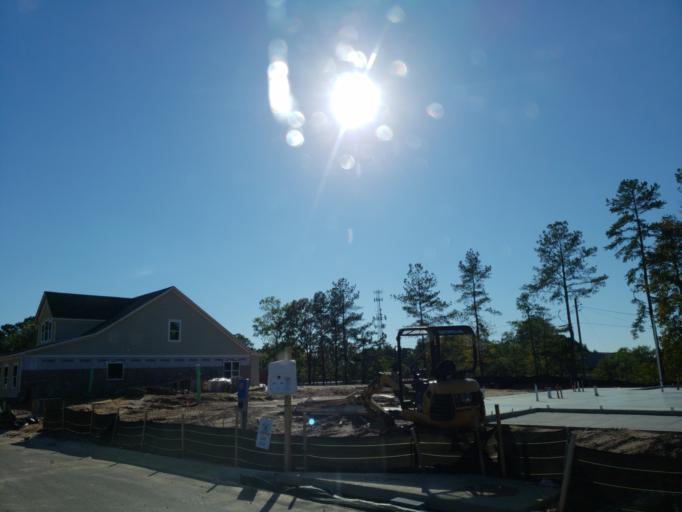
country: US
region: Georgia
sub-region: Gwinnett County
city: Lawrenceville
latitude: 33.9594
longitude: -83.9915
